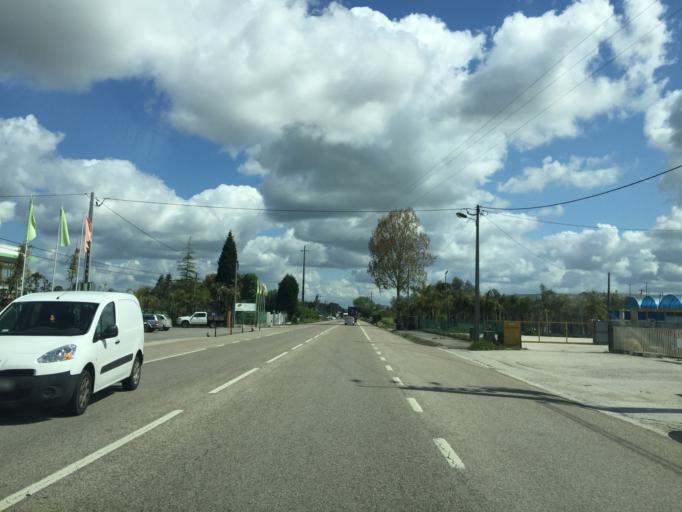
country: PT
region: Leiria
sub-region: Batalha
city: Batalha
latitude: 39.6333
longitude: -8.8506
